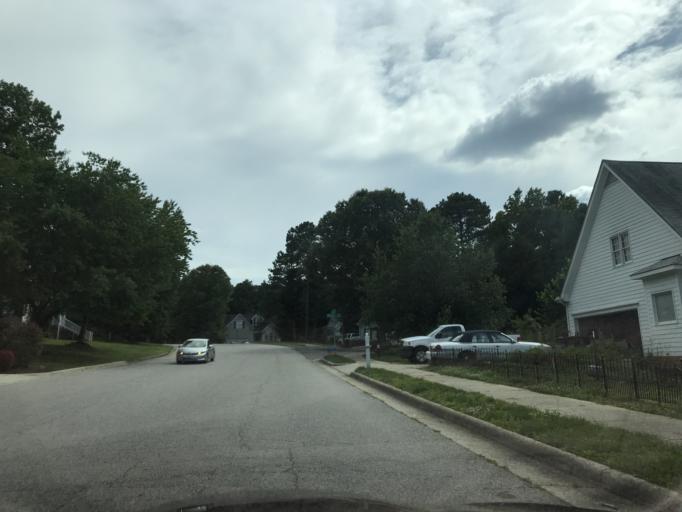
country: US
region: North Carolina
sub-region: Wake County
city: West Raleigh
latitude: 35.8748
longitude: -78.6833
